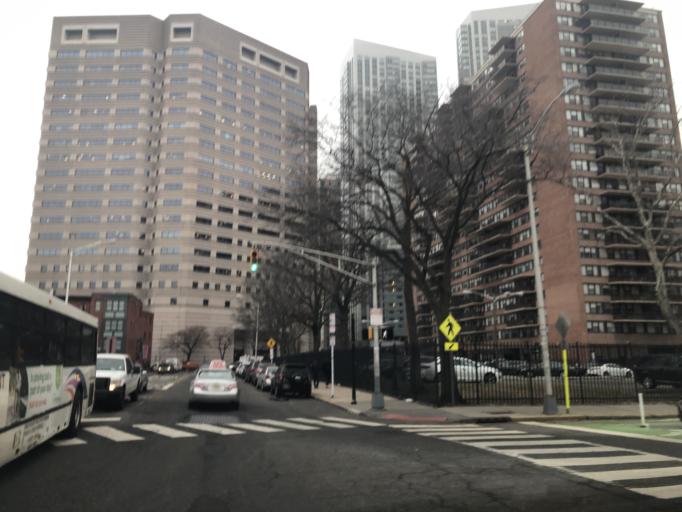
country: US
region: New Jersey
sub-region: Hudson County
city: Hoboken
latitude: 40.7173
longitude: -74.0423
